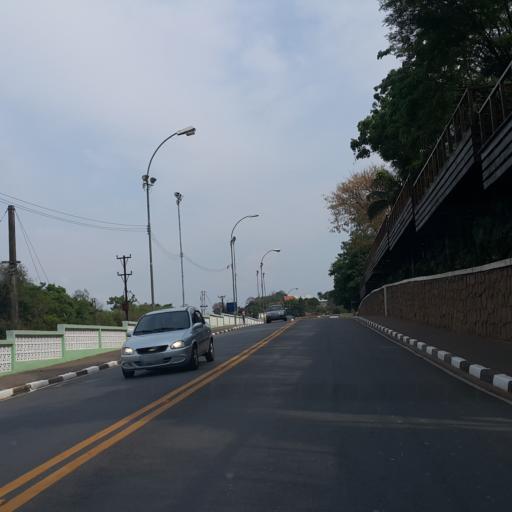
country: BR
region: Sao Paulo
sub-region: Louveira
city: Louveira
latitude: -23.0868
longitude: -46.9495
